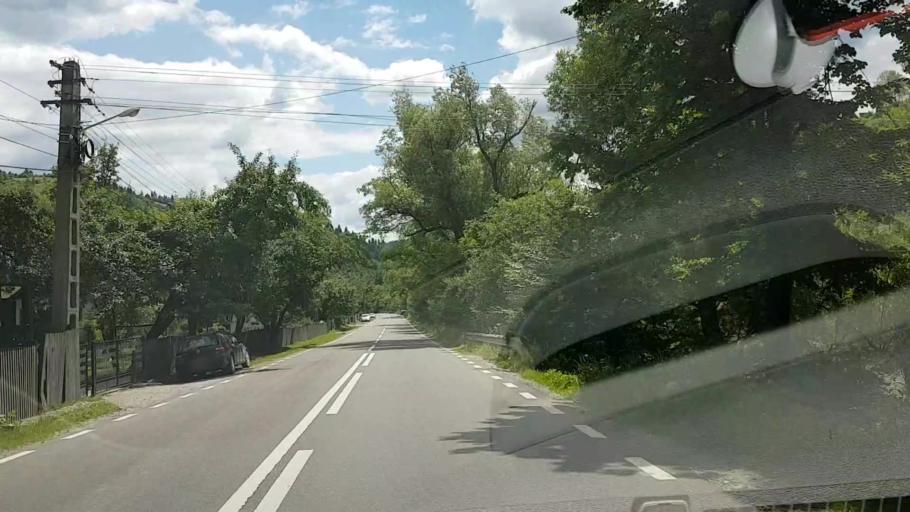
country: RO
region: Suceava
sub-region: Comuna Brosteni
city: Brosteni
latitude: 47.2582
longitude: 25.6907
